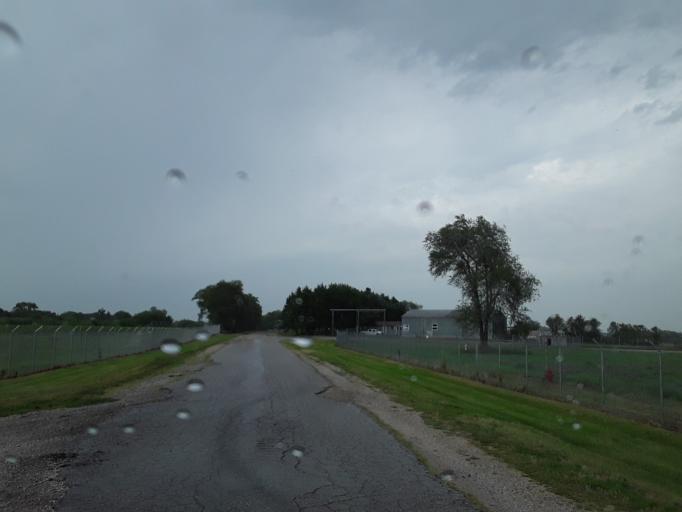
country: US
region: Nebraska
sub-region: Saunders County
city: Yutan
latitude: 41.1865
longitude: -96.4449
